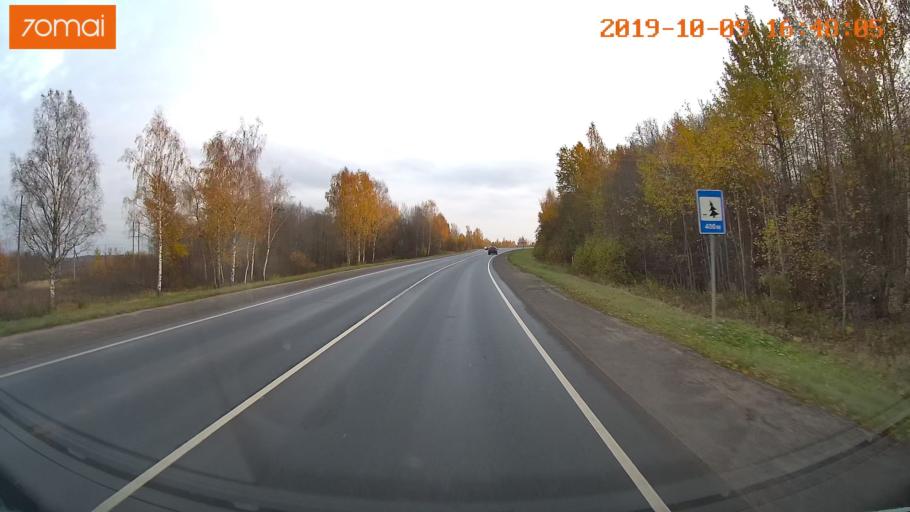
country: RU
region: Kostroma
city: Volgorechensk
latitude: 57.4316
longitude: 41.1877
